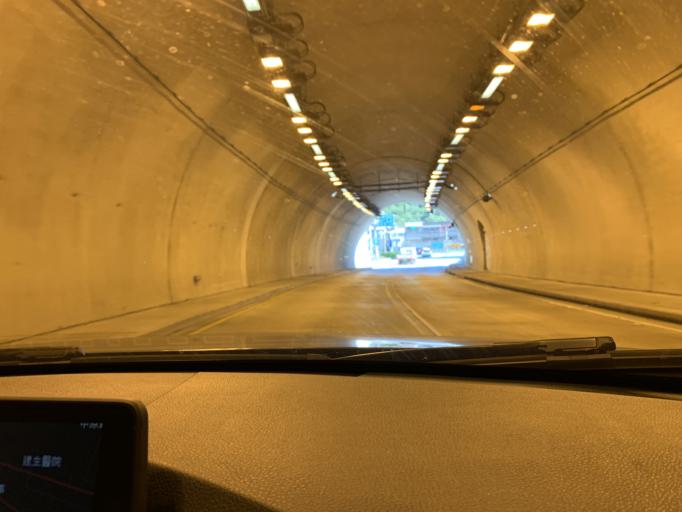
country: TW
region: Taiwan
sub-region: Yilan
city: Yilan
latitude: 24.5929
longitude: 121.8458
